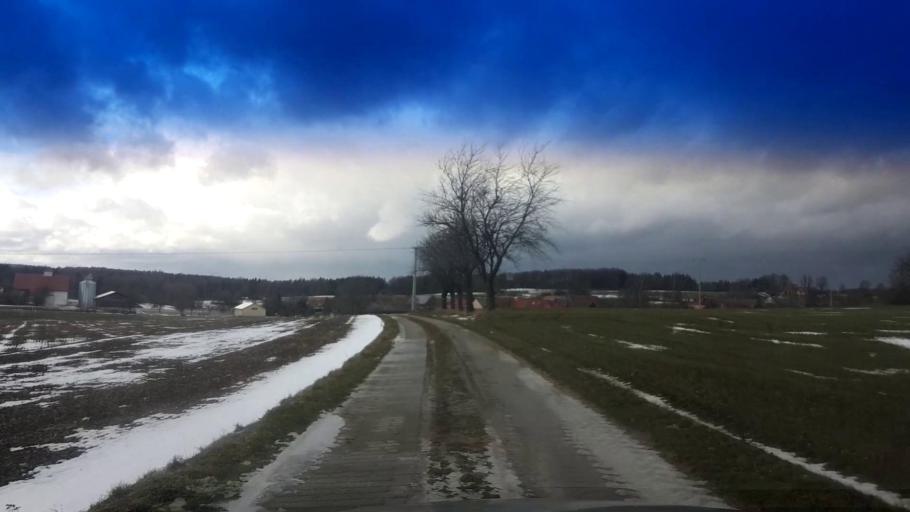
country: DE
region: Bavaria
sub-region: Upper Franconia
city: Poxdorf
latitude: 49.9336
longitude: 11.0844
